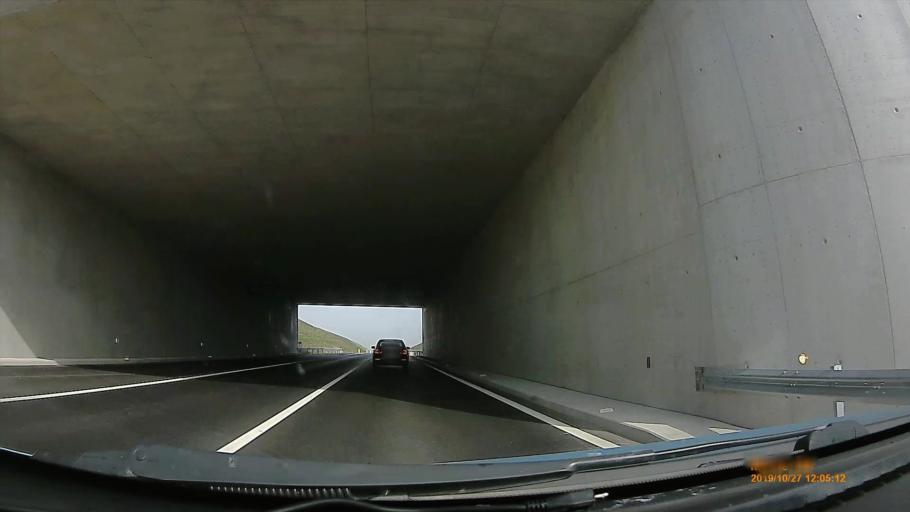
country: AT
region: Lower Austria
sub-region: Politischer Bezirk Mistelbach
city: Drasenhofen
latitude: 48.7609
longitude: 16.6356
